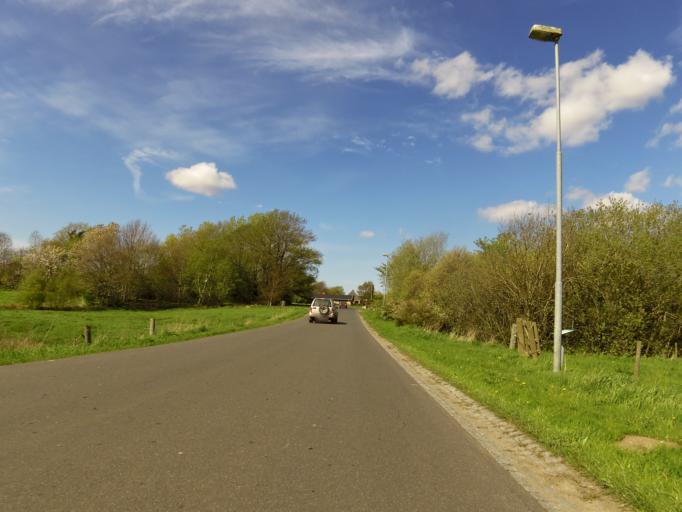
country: DK
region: Central Jutland
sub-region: Skive Kommune
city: Skive
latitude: 56.4701
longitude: 8.9699
